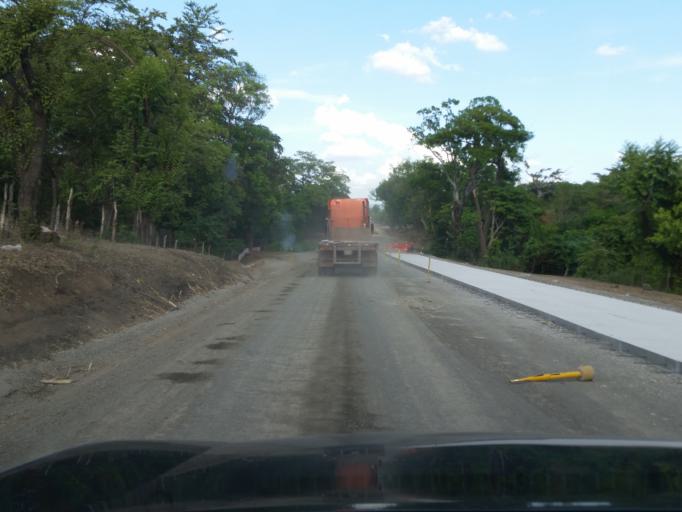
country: NI
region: Managua
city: Carlos Fonseca Amador
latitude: 12.0692
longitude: -86.4842
